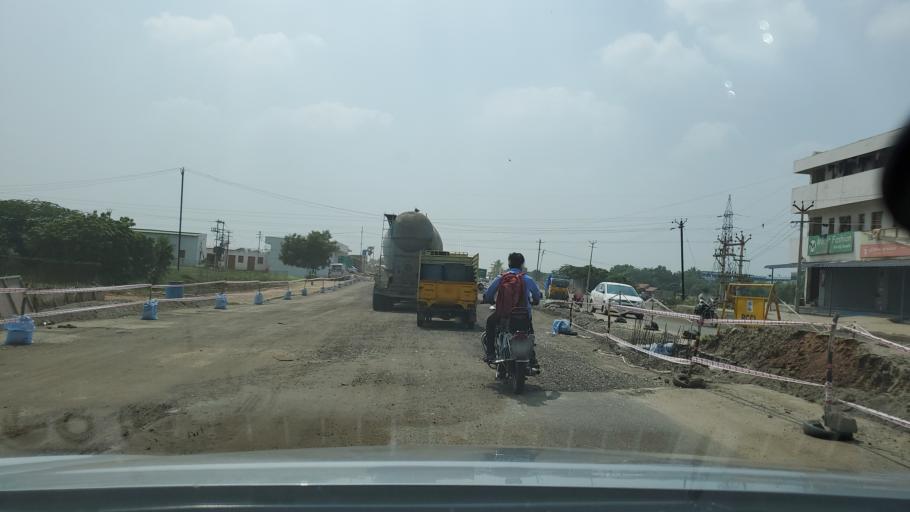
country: IN
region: Tamil Nadu
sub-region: Tiruppur
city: Kangayam
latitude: 10.9689
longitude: 77.4272
